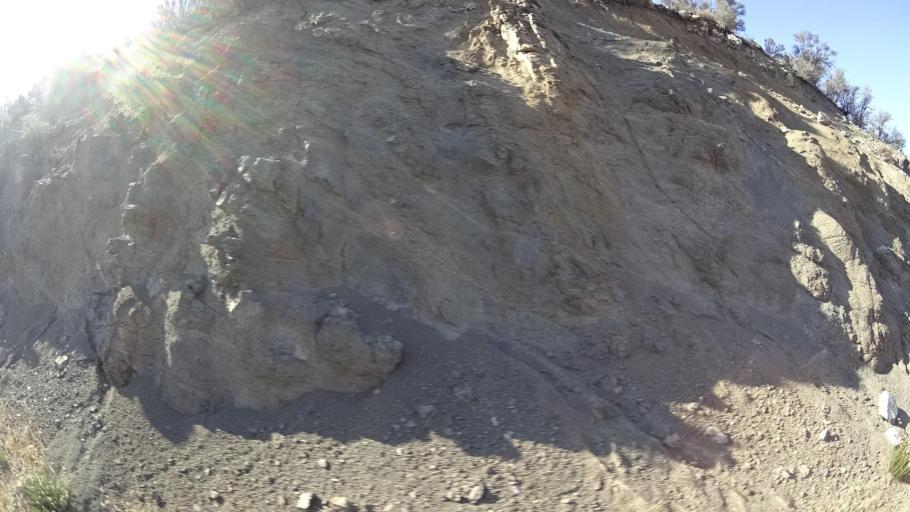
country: US
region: California
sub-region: San Diego County
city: Pine Valley
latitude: 32.8222
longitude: -116.5073
